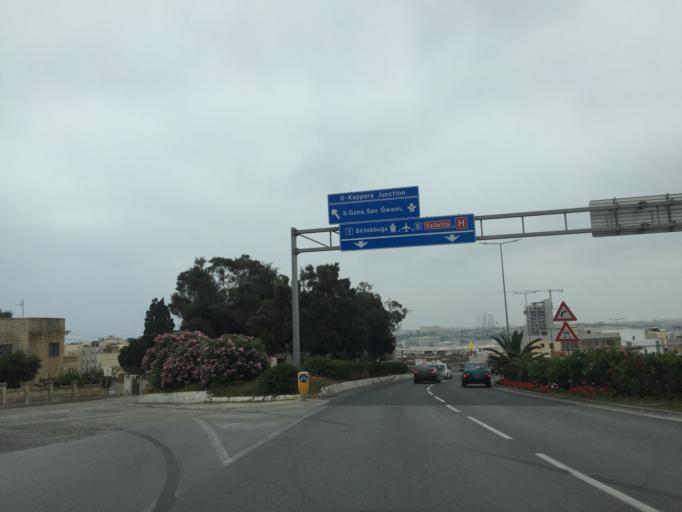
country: MT
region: Il-Gzira
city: Gzira
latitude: 35.9092
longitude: 14.4895
